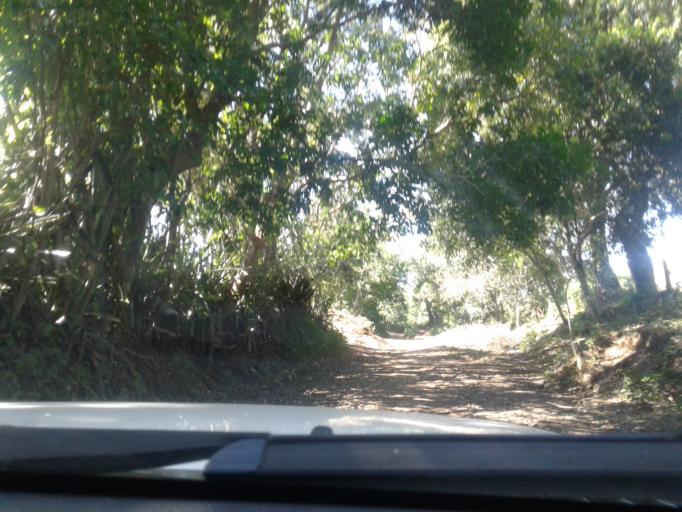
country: NI
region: Carazo
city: Santa Teresa
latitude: 11.7908
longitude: -86.1831
